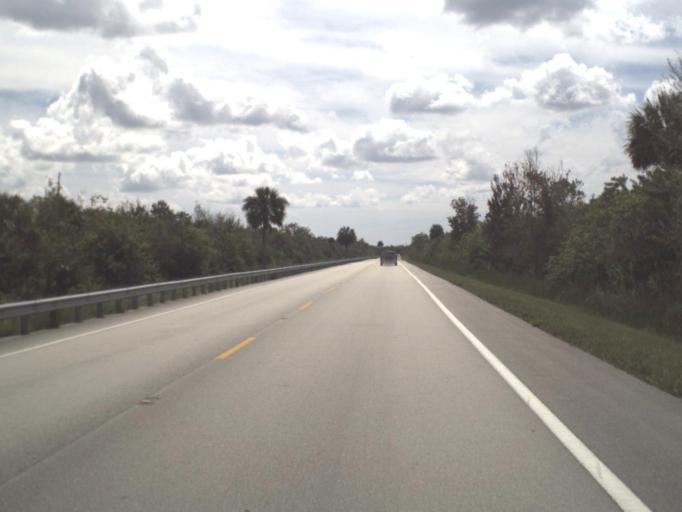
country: US
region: Florida
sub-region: Collier County
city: Lely Resort
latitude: 25.9317
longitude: -81.3575
